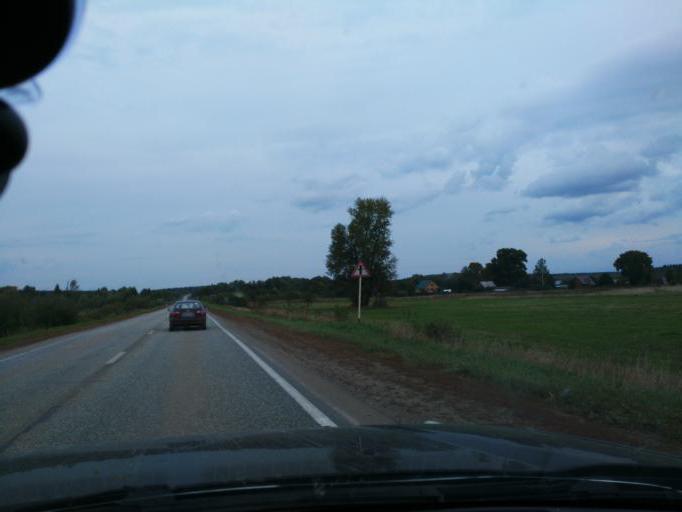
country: RU
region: Perm
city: Chernushka
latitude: 56.5120
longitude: 56.0088
